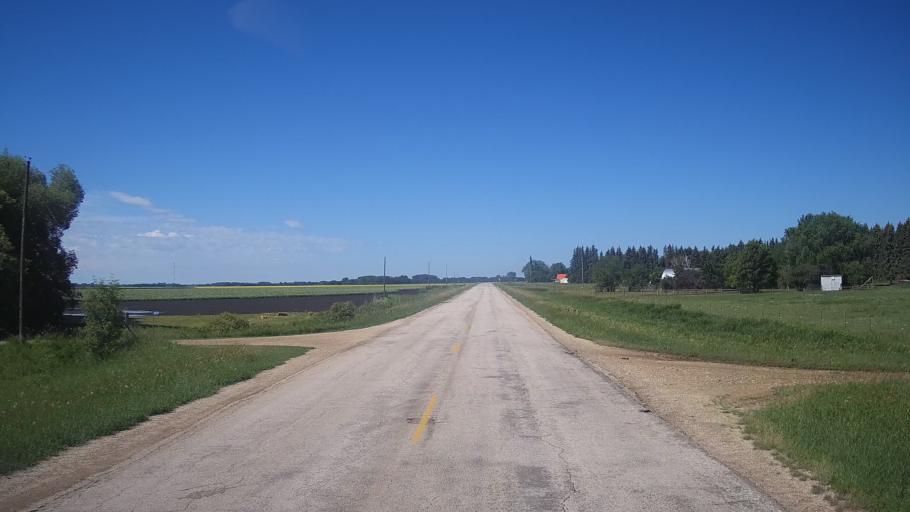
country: CA
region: Manitoba
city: Portage la Prairie
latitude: 50.0373
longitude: -98.0760
